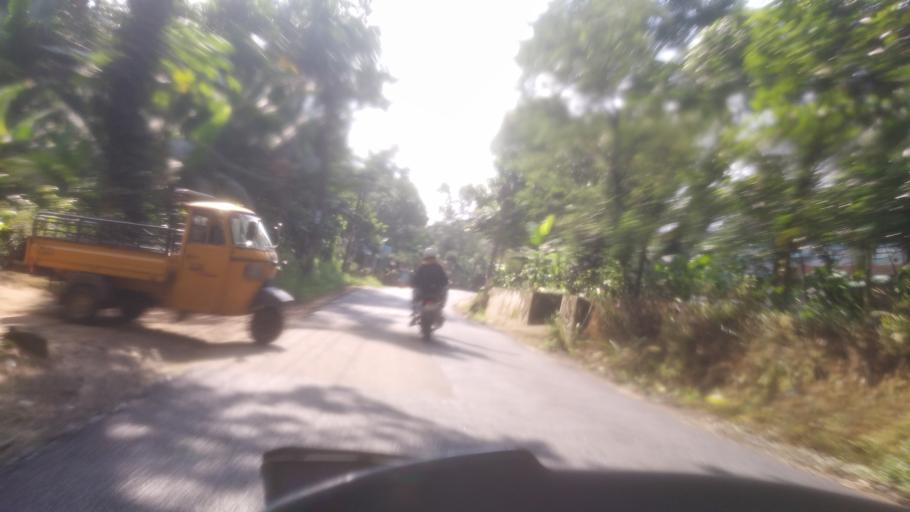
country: IN
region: Kerala
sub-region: Ernakulam
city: Kotamangalam
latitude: 10.0023
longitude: 76.7229
